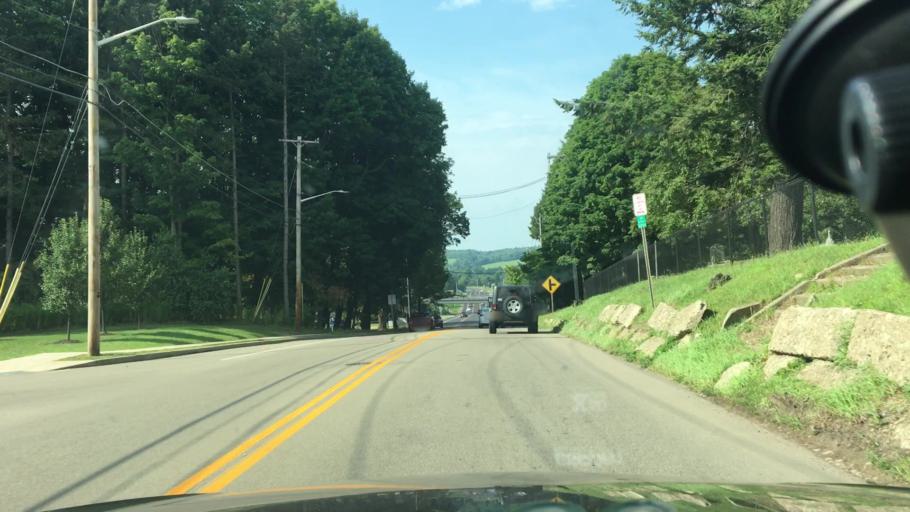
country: US
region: New York
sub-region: Chautauqua County
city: Jamestown
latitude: 42.1175
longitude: -79.2409
